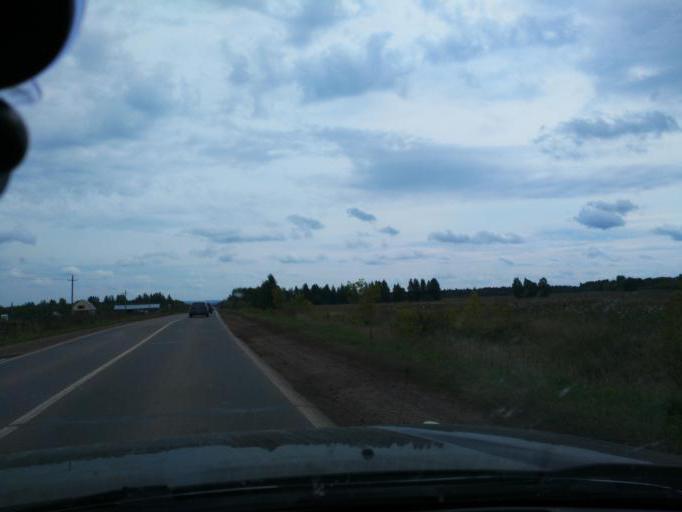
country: RU
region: Perm
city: Chernushka
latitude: 56.5083
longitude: 55.9760
